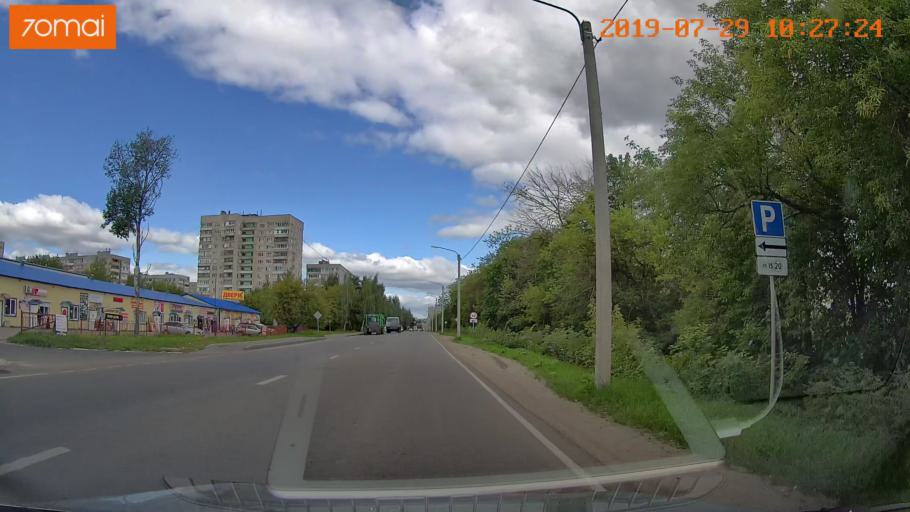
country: RU
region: Moskovskaya
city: Voskresensk
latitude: 55.3068
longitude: 38.6583
